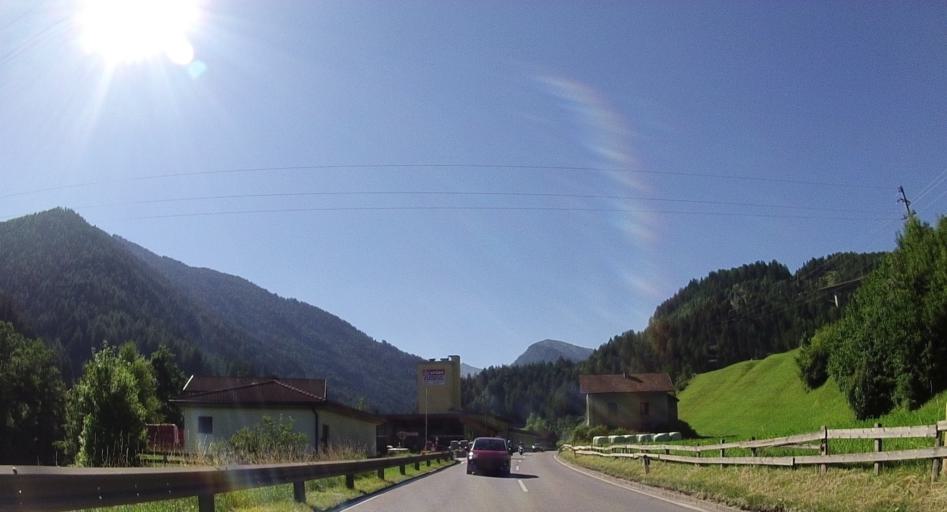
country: AT
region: Tyrol
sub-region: Politischer Bezirk Innsbruck Land
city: Steinach am Brenner
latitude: 47.0824
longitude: 11.4739
